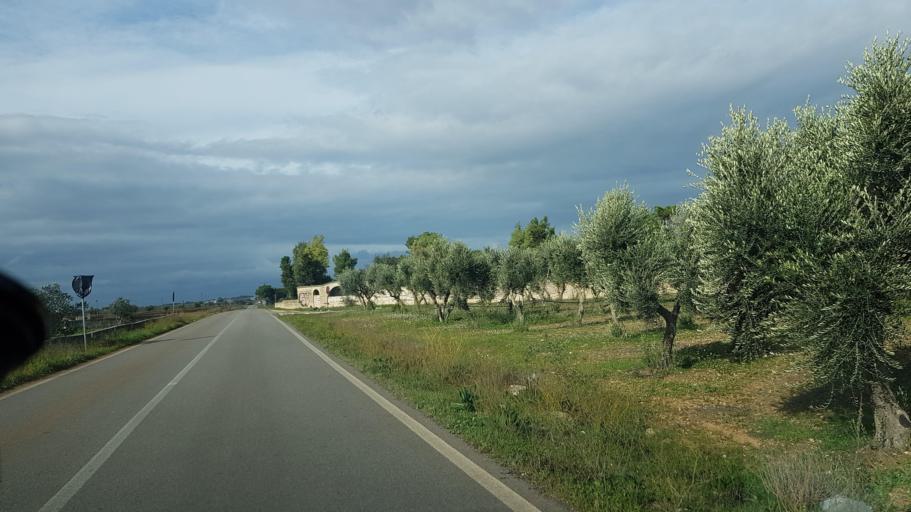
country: IT
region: Apulia
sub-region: Provincia di Brindisi
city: Torre Santa Susanna
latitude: 40.4783
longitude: 17.6946
